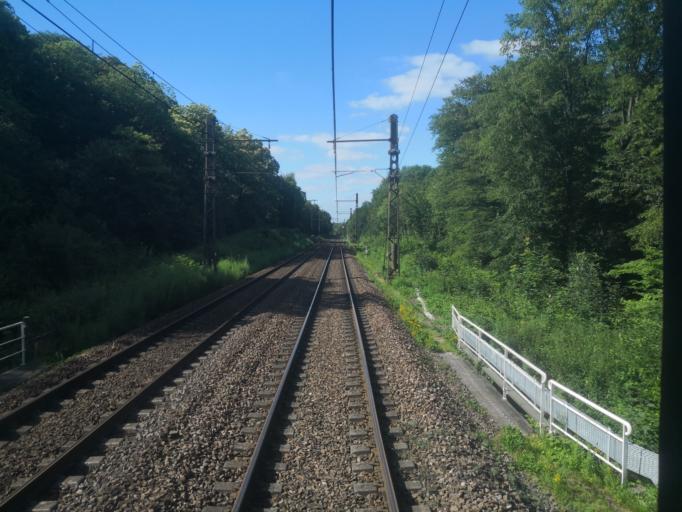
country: FR
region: Ile-de-France
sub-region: Departement de Seine-et-Marne
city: La Rochette
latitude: 48.5014
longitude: 2.6682
